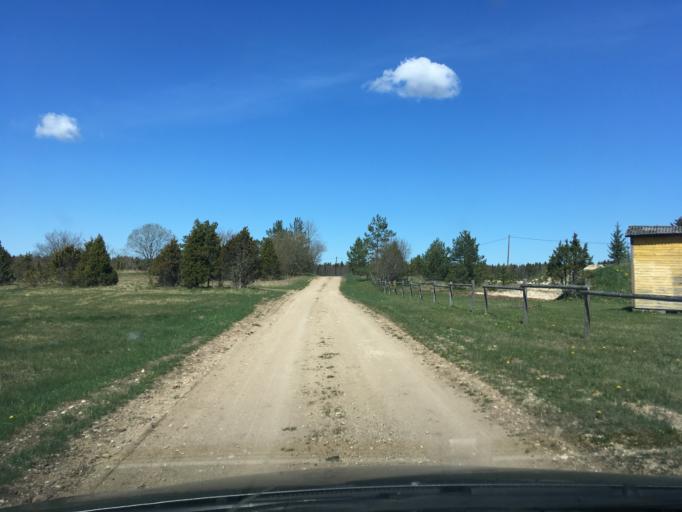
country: EE
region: Harju
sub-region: Raasiku vald
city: Raasiku
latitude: 59.2211
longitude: 25.1529
